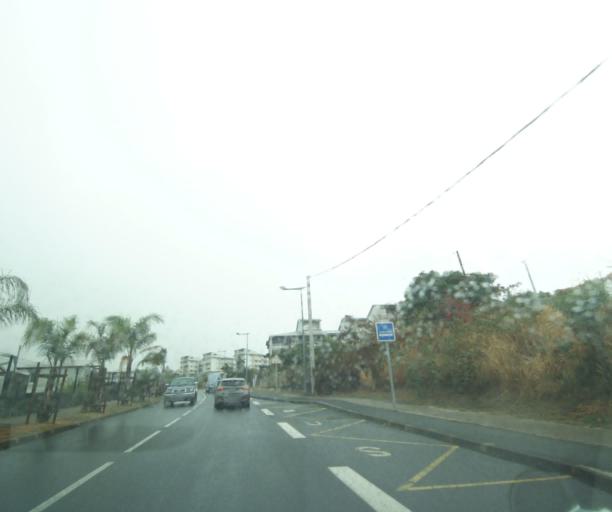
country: RE
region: Reunion
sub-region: Reunion
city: Saint-Paul
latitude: -21.0454
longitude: 55.2591
